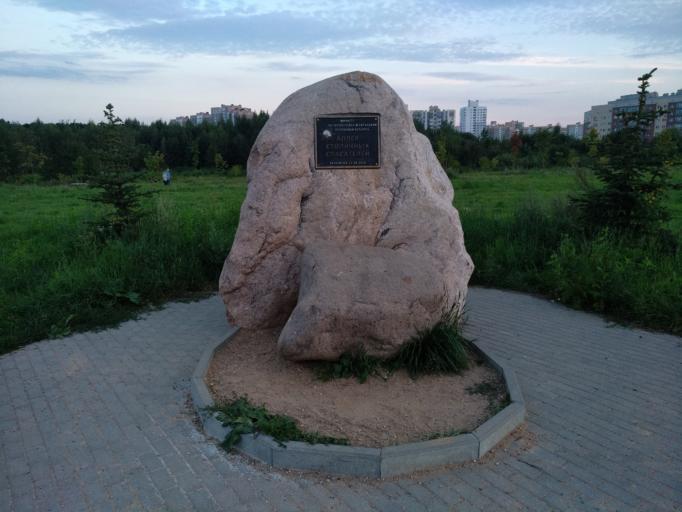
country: BY
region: Minsk
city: Novoye Medvezhino
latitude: 53.8954
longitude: 27.4278
